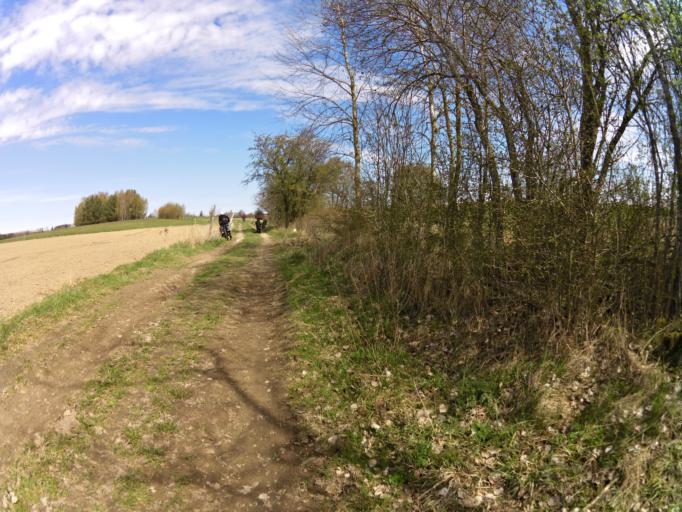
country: PL
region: West Pomeranian Voivodeship
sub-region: Powiat szczecinecki
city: Szczecinek
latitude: 53.7713
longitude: 16.6259
